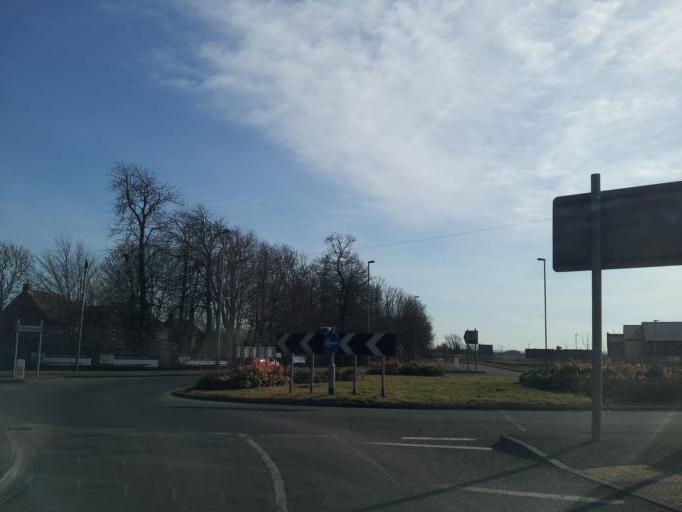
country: GB
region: England
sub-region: Nottinghamshire
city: Newark on Trent
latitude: 53.0435
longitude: -0.7722
